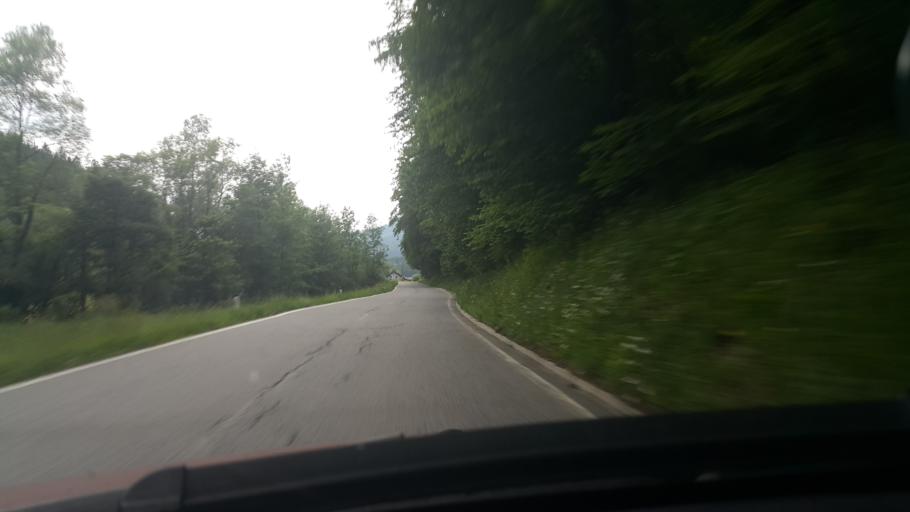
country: AT
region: Styria
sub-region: Politischer Bezirk Graz-Umgebung
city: Stiwoll
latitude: 47.0952
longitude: 15.2209
